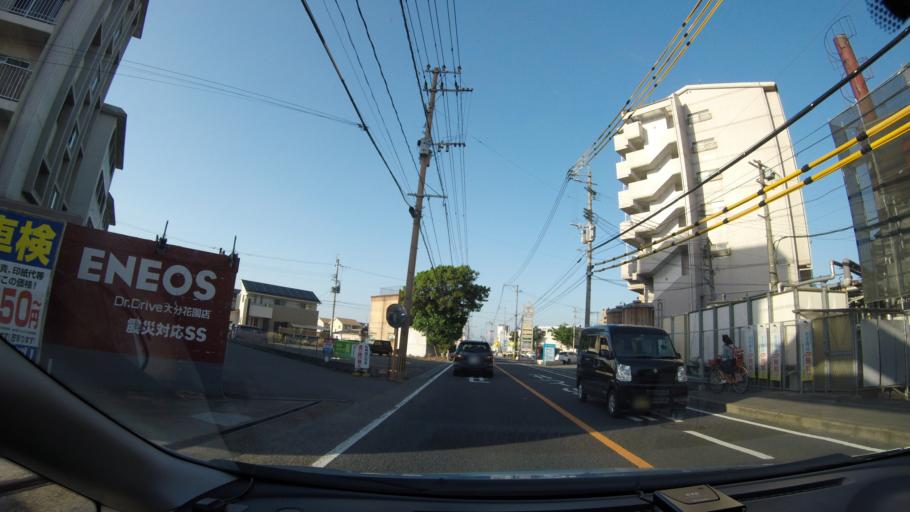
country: JP
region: Oita
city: Oita
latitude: 33.2090
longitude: 131.6054
